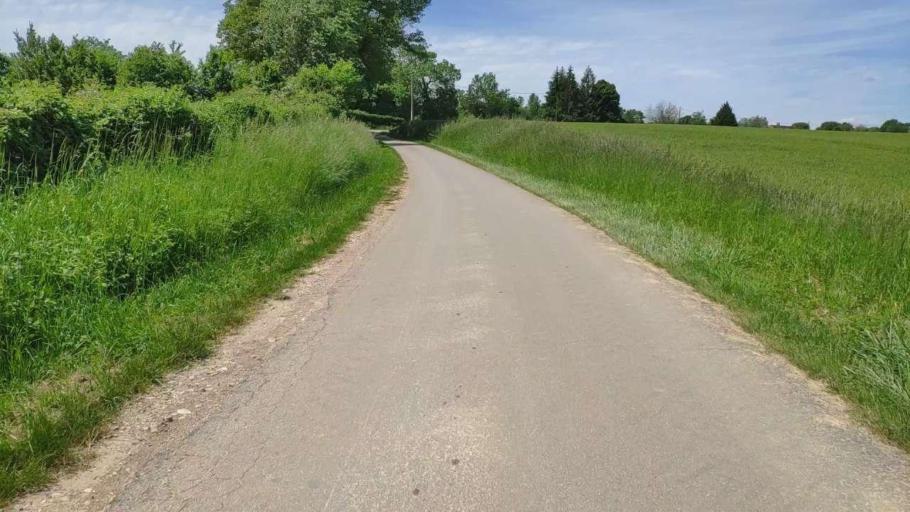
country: FR
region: Franche-Comte
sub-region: Departement du Jura
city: Bletterans
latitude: 46.7807
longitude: 5.3829
